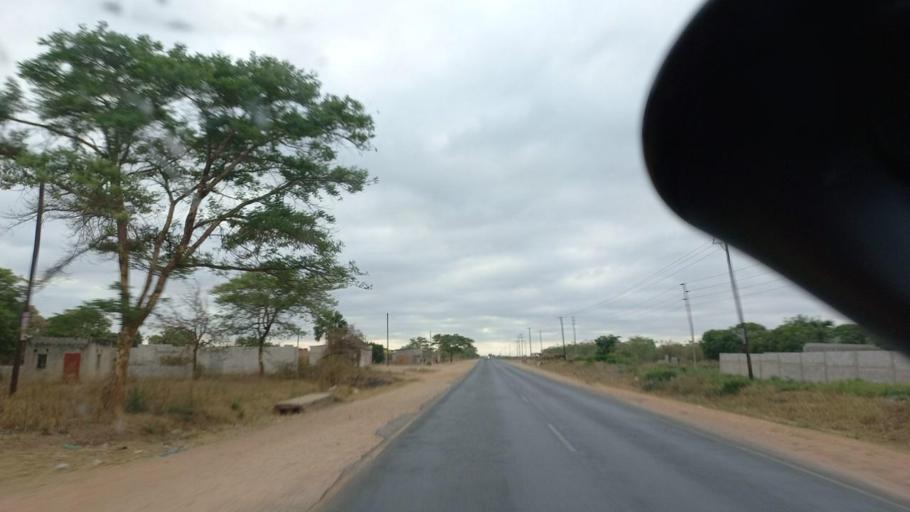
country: ZM
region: Lusaka
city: Chongwe
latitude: -15.3423
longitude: 28.6440
